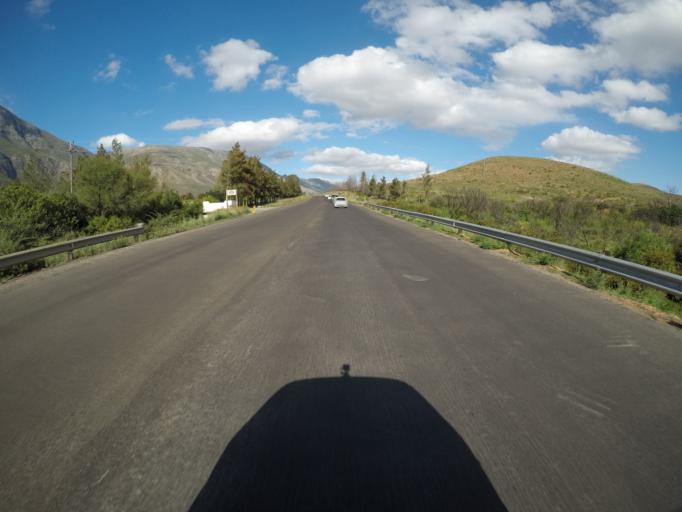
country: ZA
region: Western Cape
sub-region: Cape Winelands District Municipality
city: Ashton
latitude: -33.8706
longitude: 20.1406
